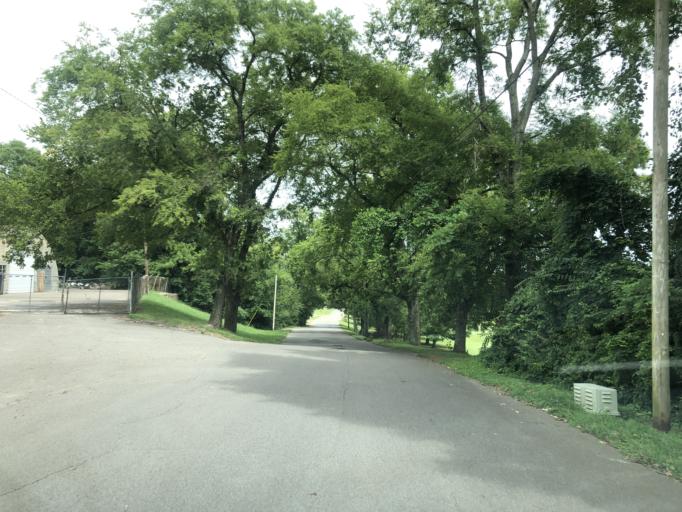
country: US
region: Tennessee
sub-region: Davidson County
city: Nashville
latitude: 36.1659
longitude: -86.7369
